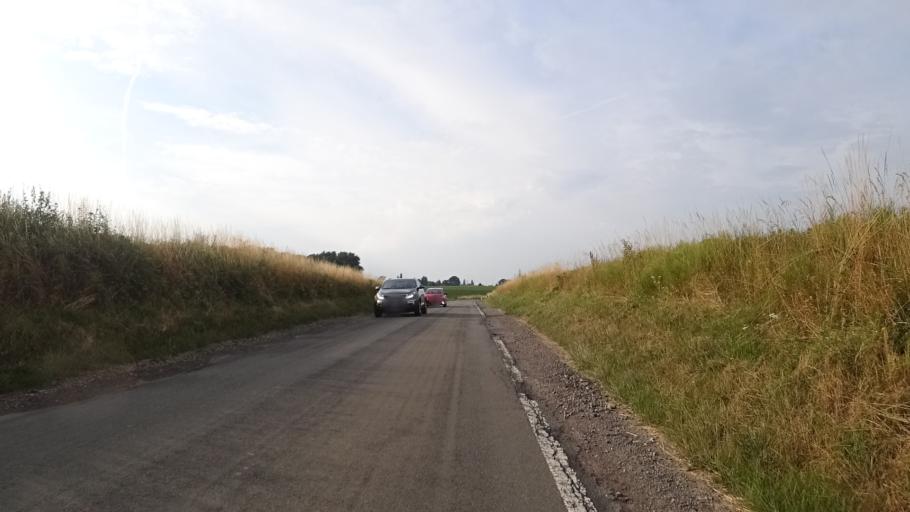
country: BE
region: Wallonia
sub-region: Province du Brabant Wallon
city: Perwez
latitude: 50.5861
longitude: 4.8283
